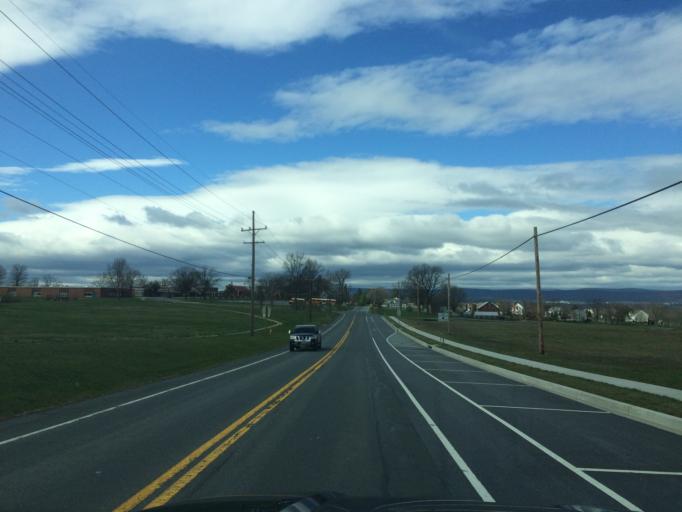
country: US
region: Maryland
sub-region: Frederick County
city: Jefferson
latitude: 39.3606
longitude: -77.5444
